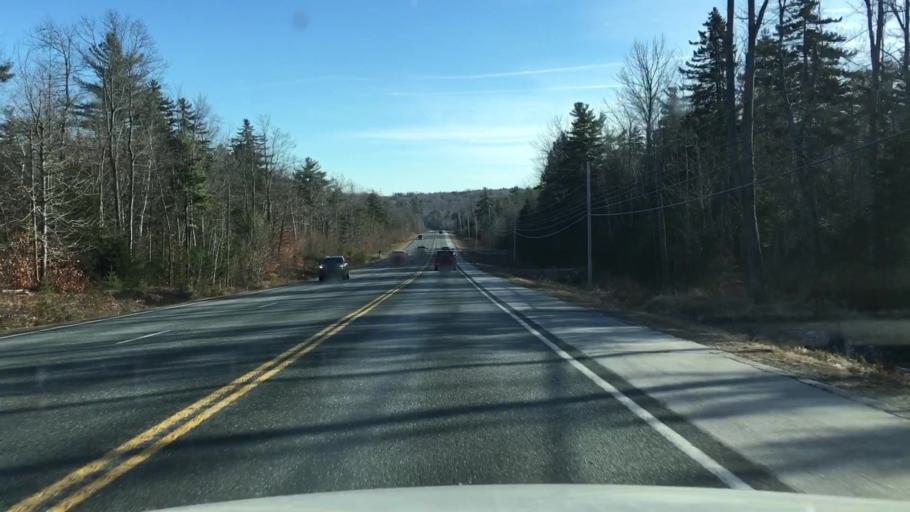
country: US
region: Maine
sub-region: Hancock County
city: Dedham
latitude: 44.6410
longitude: -68.5521
